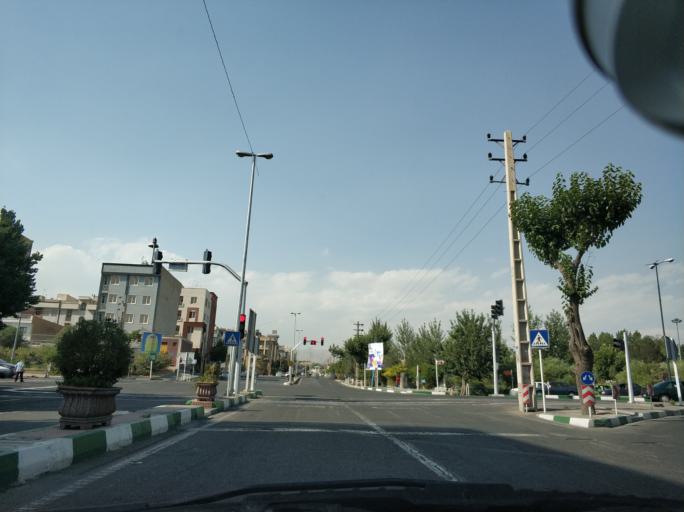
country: IR
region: Tehran
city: Tajrish
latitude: 35.7579
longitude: 51.5401
